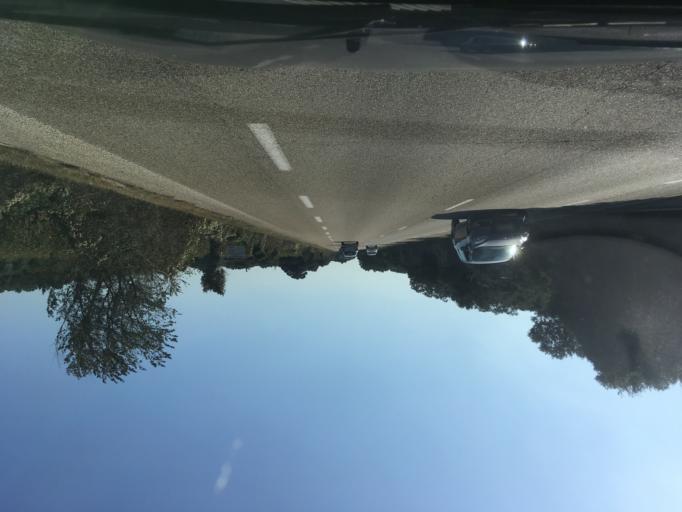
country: FR
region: Languedoc-Roussillon
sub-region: Departement du Gard
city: Pujaut
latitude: 44.0153
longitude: 4.7393
